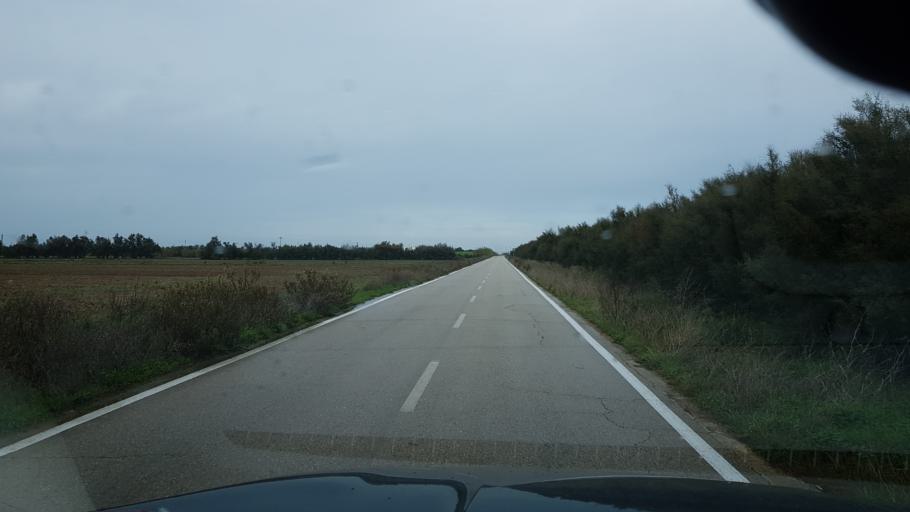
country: IT
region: Apulia
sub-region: Provincia di Brindisi
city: Brindisi
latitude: 40.6835
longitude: 17.8464
